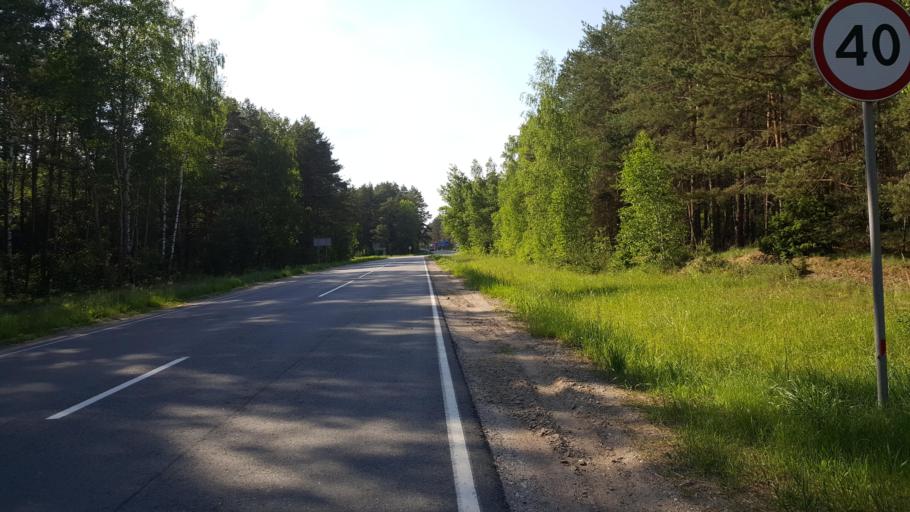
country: BY
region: Brest
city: Zhabinka
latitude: 52.3784
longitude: 24.1246
